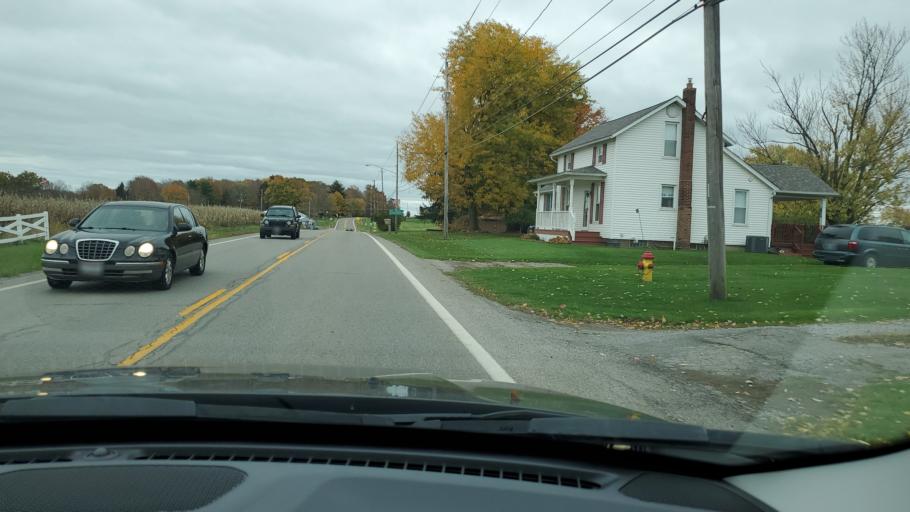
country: US
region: Ohio
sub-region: Mahoning County
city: New Middletown
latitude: 40.9154
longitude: -80.6020
